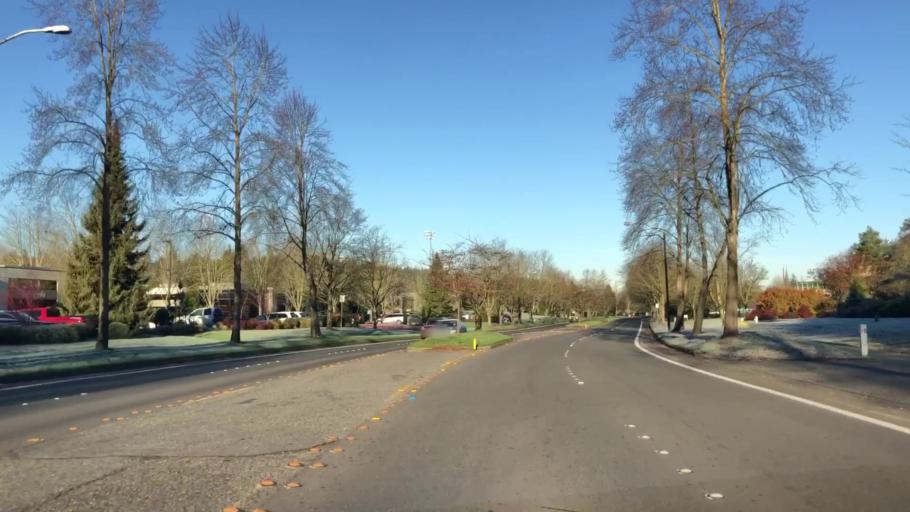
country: US
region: Washington
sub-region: King County
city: Woodinville
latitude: 47.7647
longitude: -122.1782
